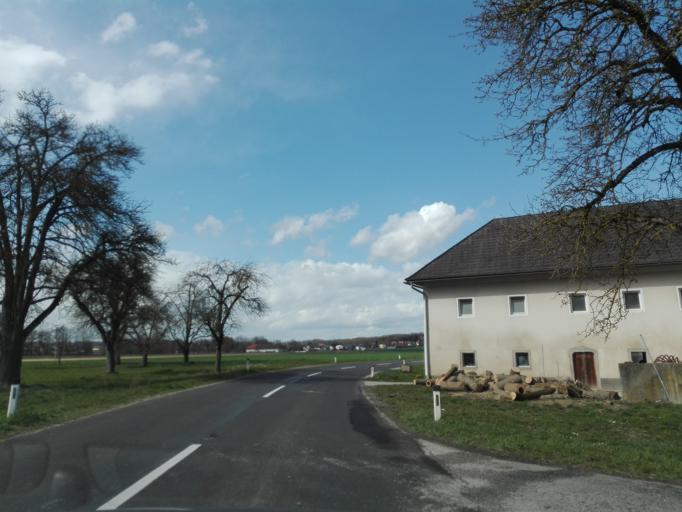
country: AT
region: Upper Austria
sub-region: Wels-Land
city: Holzhausen
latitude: 48.2223
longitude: 14.1271
